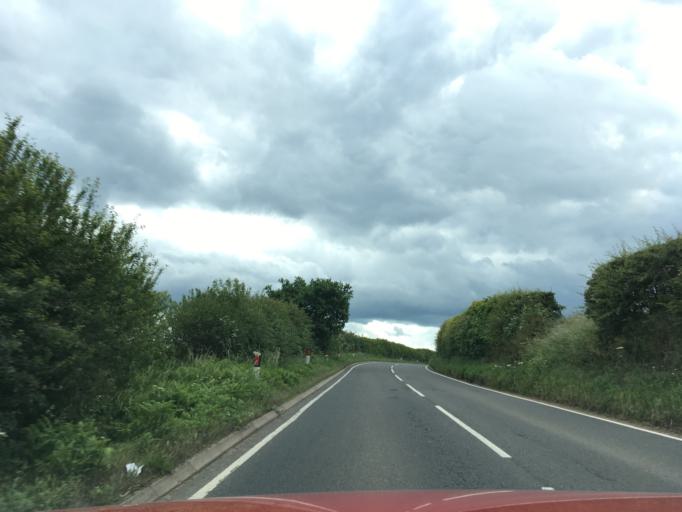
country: GB
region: England
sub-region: Central Bedfordshire
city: Woburn
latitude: 51.9803
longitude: -0.6381
